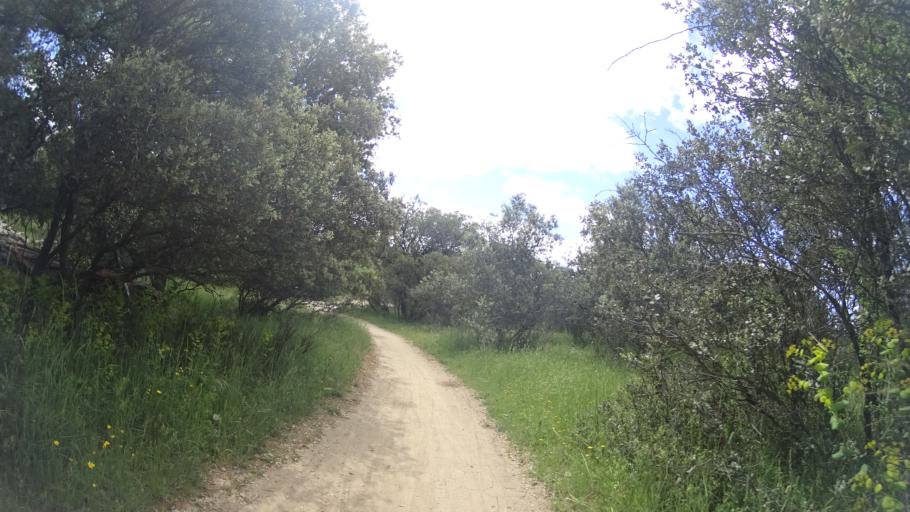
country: ES
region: Madrid
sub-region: Provincia de Madrid
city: Brunete
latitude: 40.4023
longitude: -3.9445
